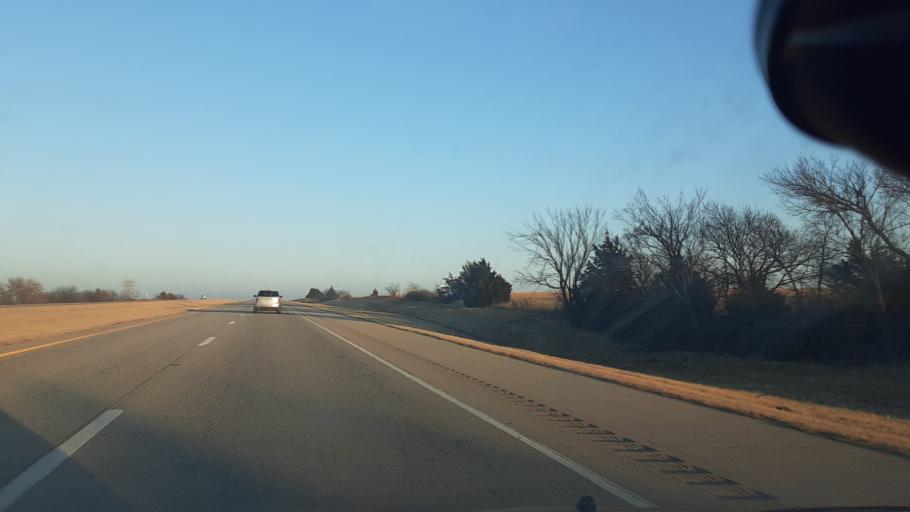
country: US
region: Oklahoma
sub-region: Noble County
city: Perry
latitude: 36.3978
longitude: -97.4418
